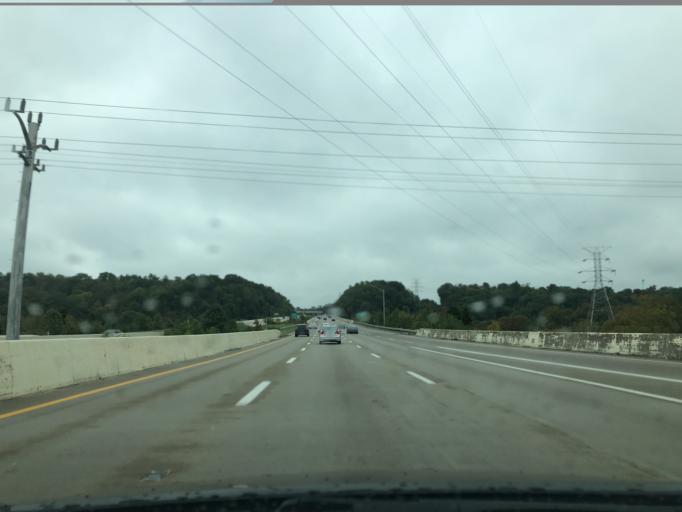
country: US
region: Ohio
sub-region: Hamilton County
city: The Village of Indian Hill
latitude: 39.2411
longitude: -84.2997
